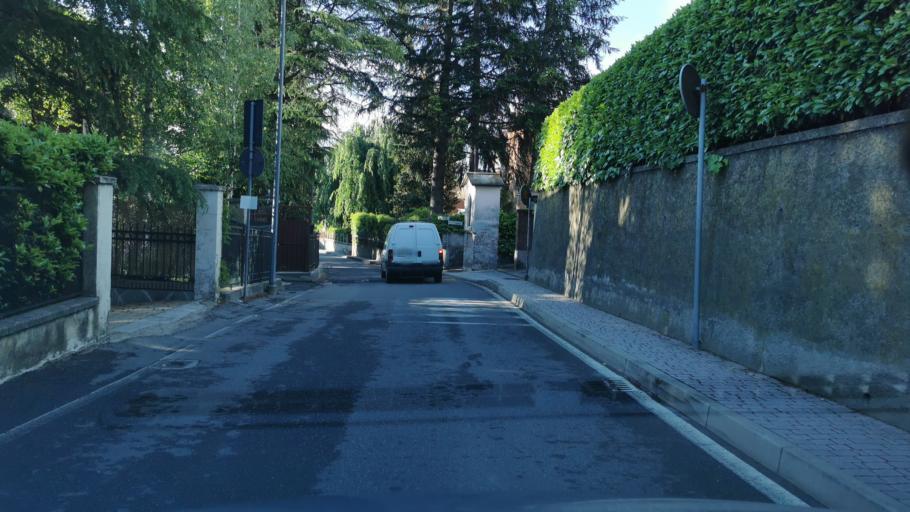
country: IT
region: Piedmont
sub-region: Provincia di Torino
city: Pino Torinese
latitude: 45.0382
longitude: 7.7729
